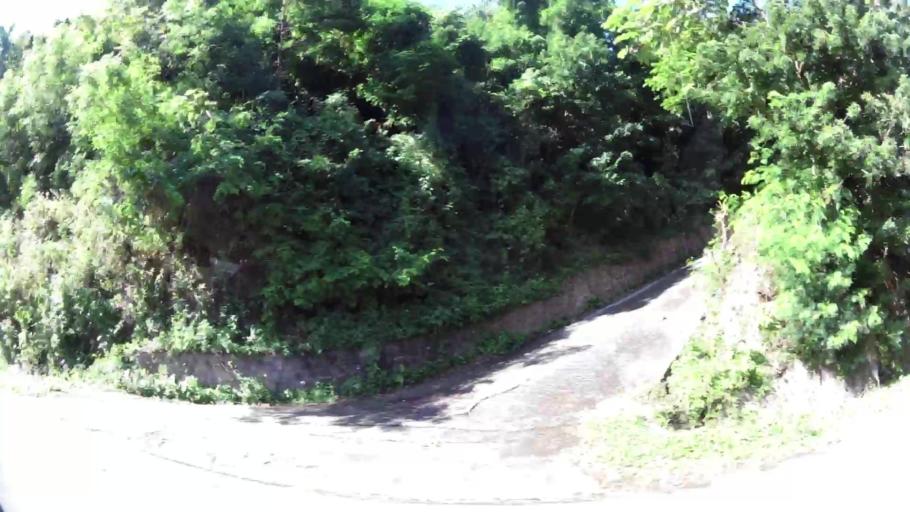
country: LC
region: Soufriere
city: Soufriere
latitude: 13.8353
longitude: -61.0539
